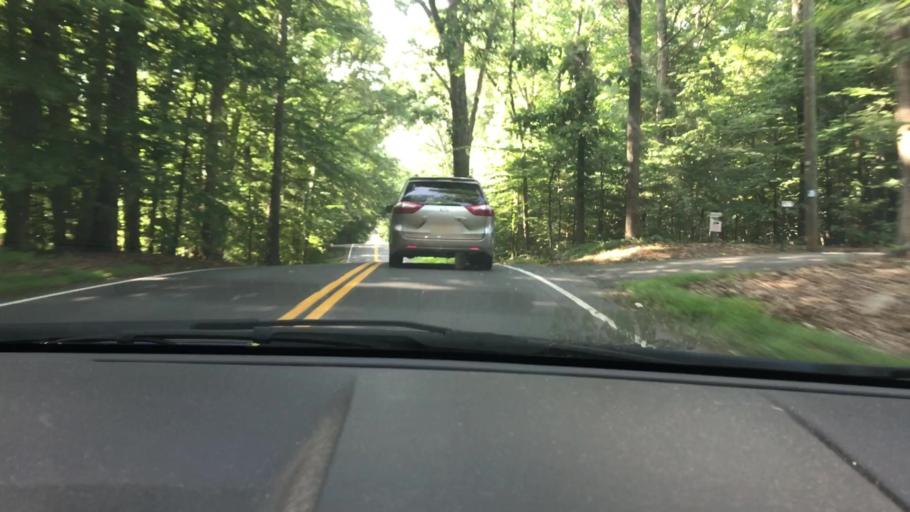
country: US
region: Virginia
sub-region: Fairfax County
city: Great Falls
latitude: 39.0064
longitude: -77.2651
